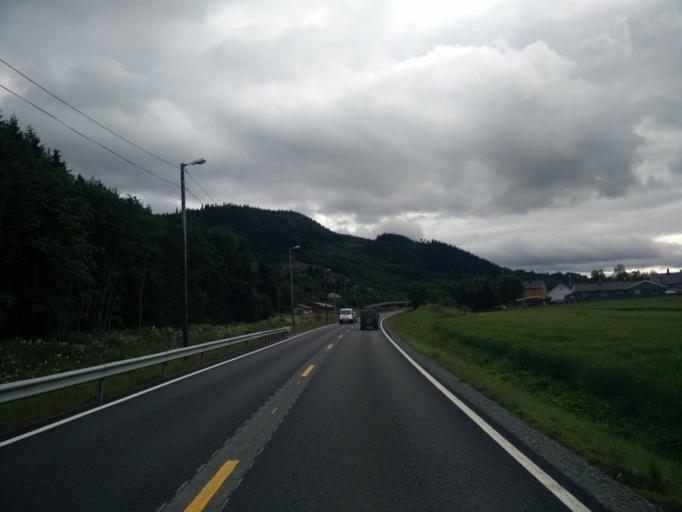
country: NO
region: Sor-Trondelag
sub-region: Orkdal
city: Orkanger
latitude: 63.2903
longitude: 9.8521
